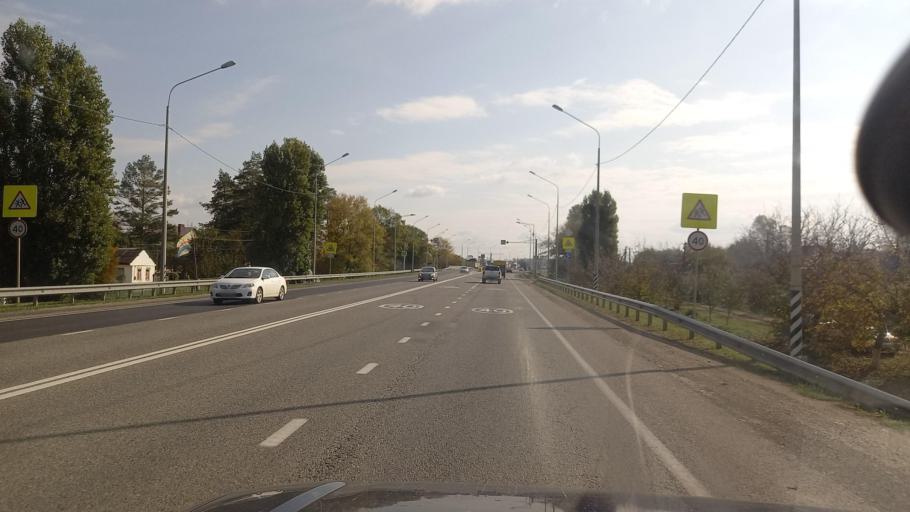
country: RU
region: Krasnodarskiy
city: Novoukrainskiy
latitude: 44.8953
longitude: 38.0568
